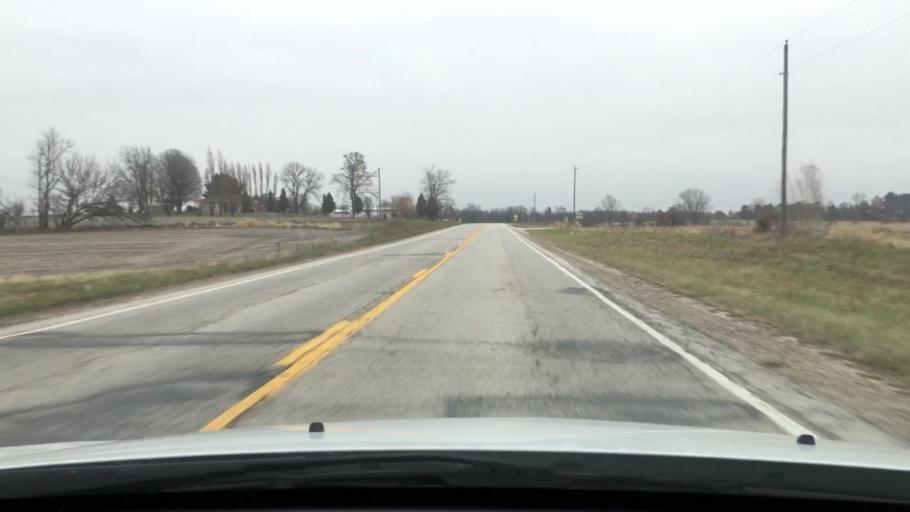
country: US
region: Illinois
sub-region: Pike County
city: Pittsfield
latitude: 39.5865
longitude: -90.8999
